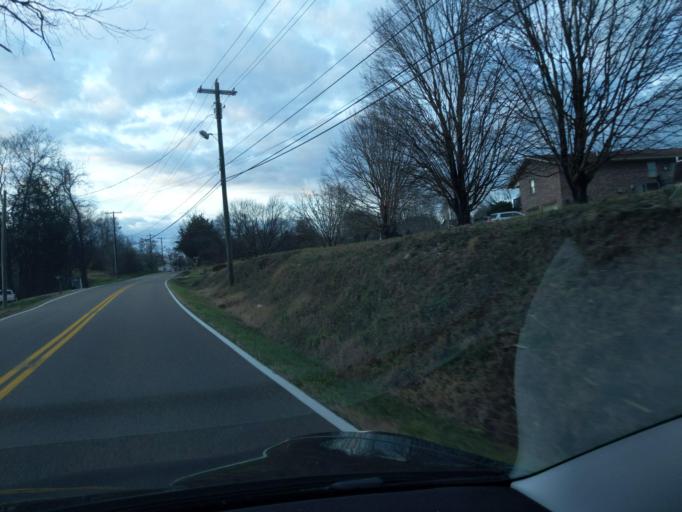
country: US
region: Tennessee
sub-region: Jefferson County
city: Dandridge
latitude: 36.0265
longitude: -83.4085
